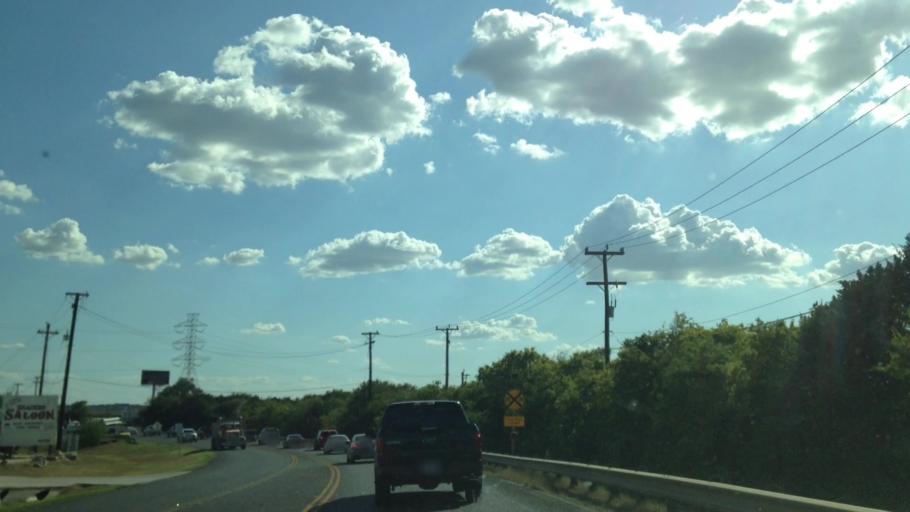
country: US
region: Texas
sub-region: Comal County
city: Garden Ridge
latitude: 29.6109
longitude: -98.3241
